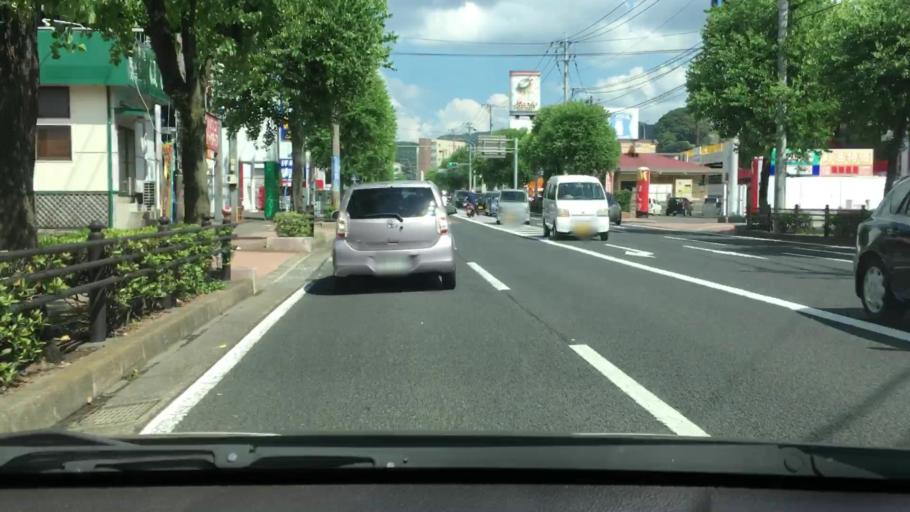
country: JP
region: Nagasaki
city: Sasebo
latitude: 33.2082
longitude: 129.7168
